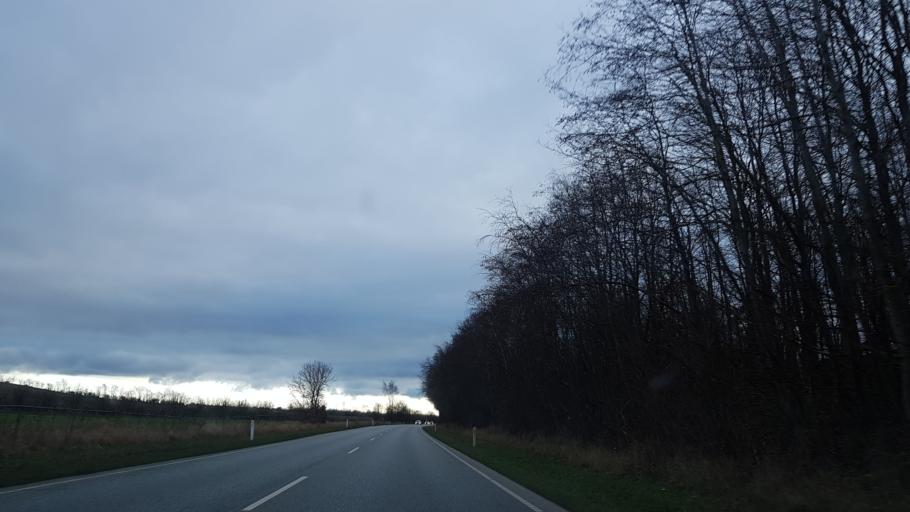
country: DK
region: Zealand
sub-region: Odsherred Kommune
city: Hojby
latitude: 55.9070
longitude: 11.5548
